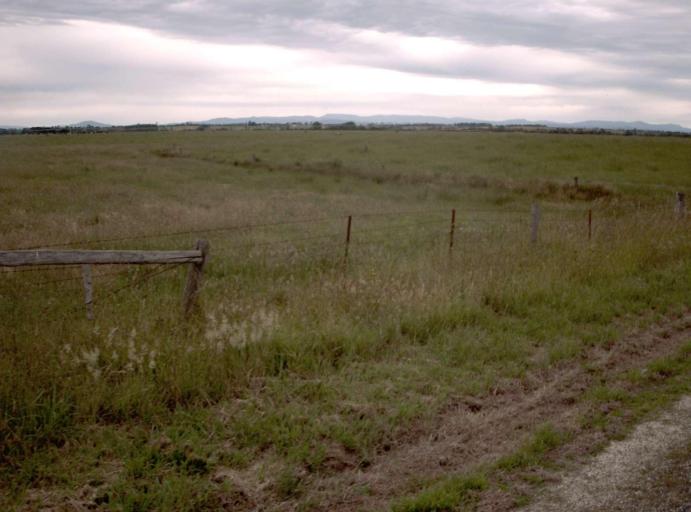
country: AU
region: Victoria
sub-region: Wellington
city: Sale
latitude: -38.0388
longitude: 147.1767
